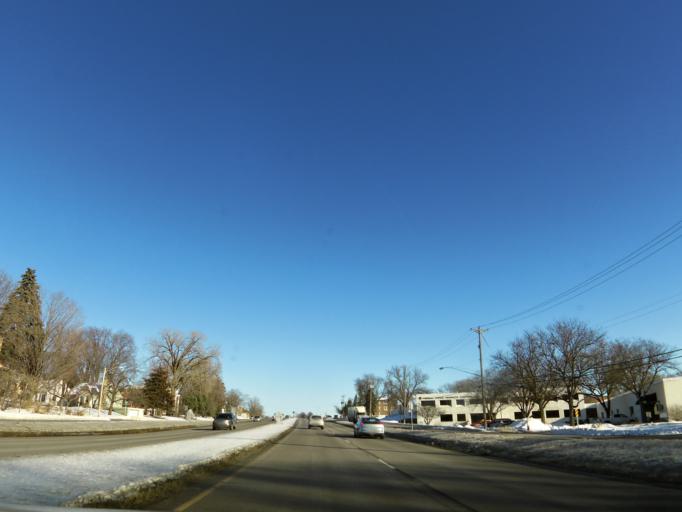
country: US
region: Minnesota
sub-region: Hennepin County
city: Saint Louis Park
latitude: 44.9462
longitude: -93.3387
